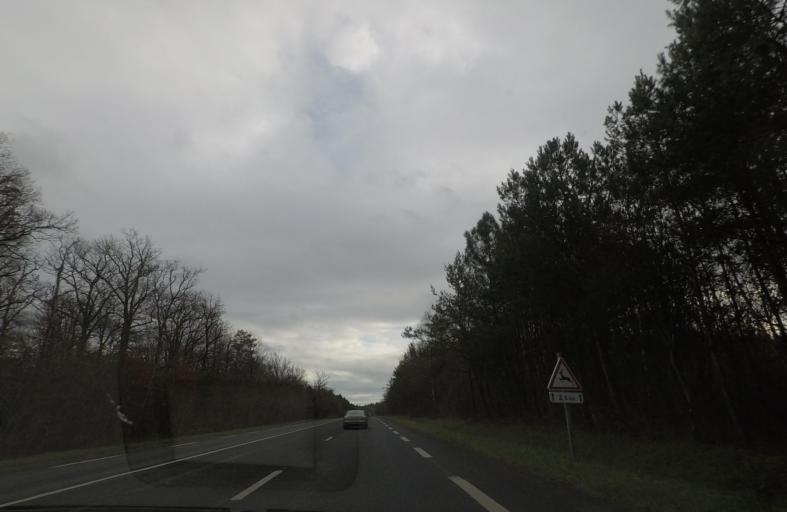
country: FR
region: Centre
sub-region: Departement du Loir-et-Cher
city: Mur-de-Sologne
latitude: 47.3959
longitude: 1.6438
